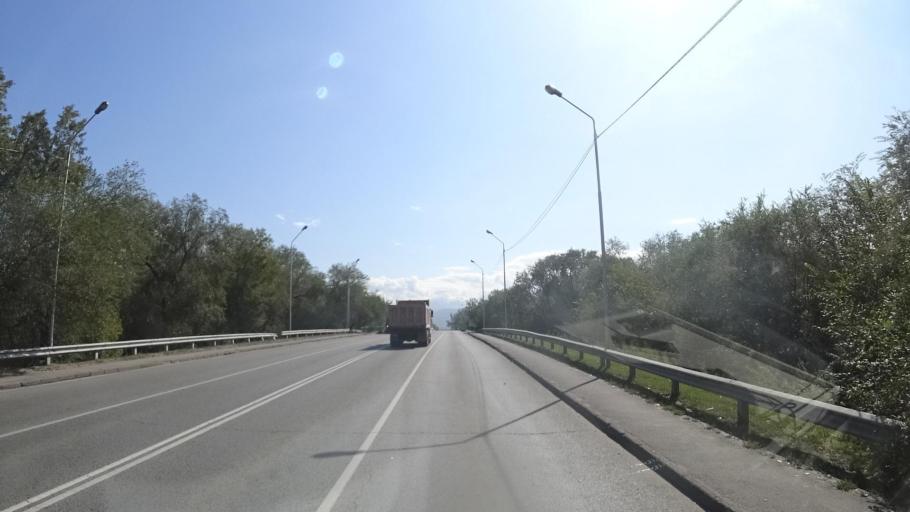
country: KZ
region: Almaty Oblysy
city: Pervomayskiy
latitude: 43.3429
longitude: 76.9764
